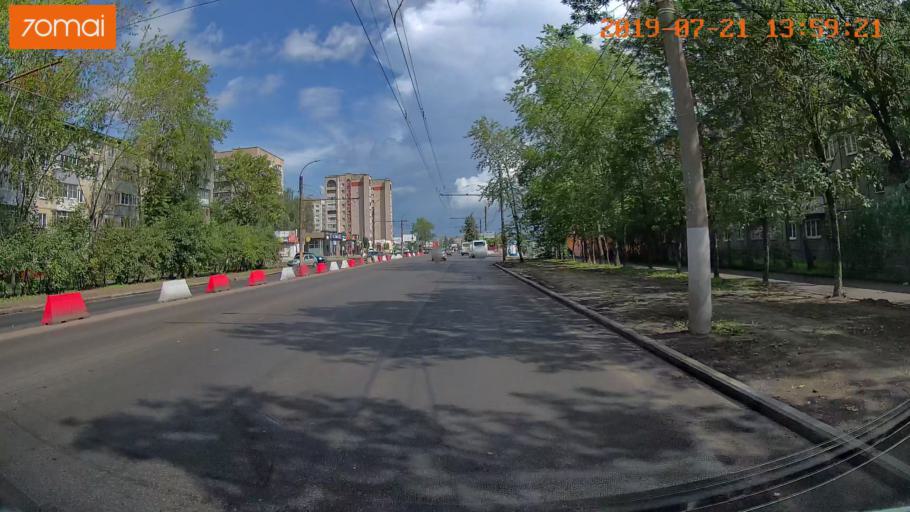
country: RU
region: Ivanovo
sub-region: Gorod Ivanovo
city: Ivanovo
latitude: 56.9574
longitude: 40.9917
